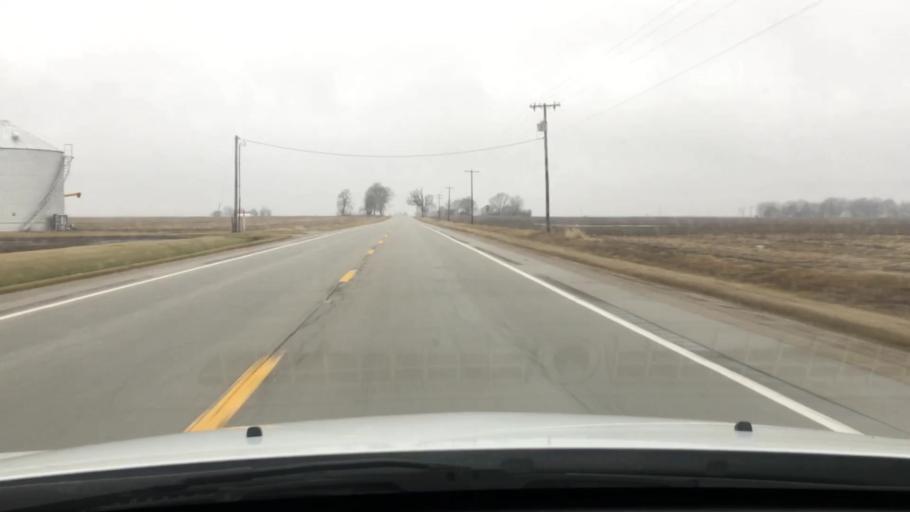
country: US
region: Illinois
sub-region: Livingston County
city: Flanagan
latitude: 40.8722
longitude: -88.7669
